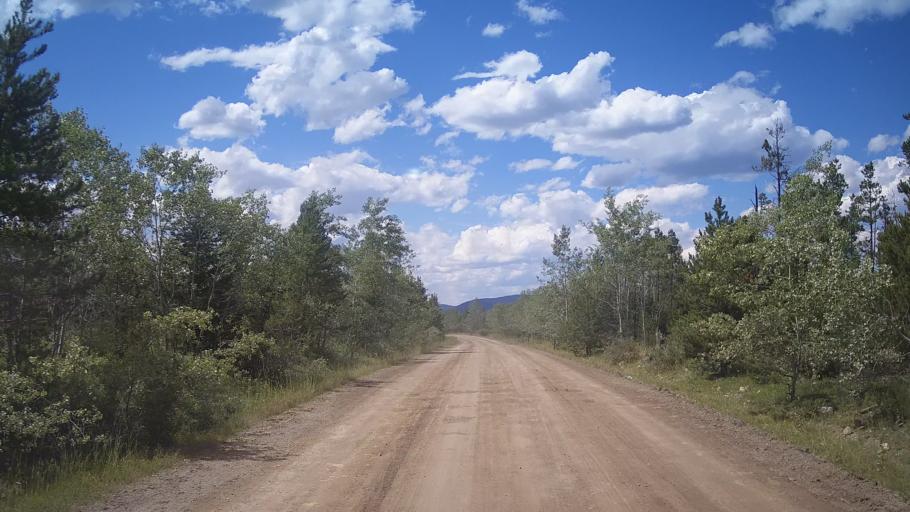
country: CA
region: British Columbia
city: Lillooet
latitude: 51.3406
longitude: -121.9222
